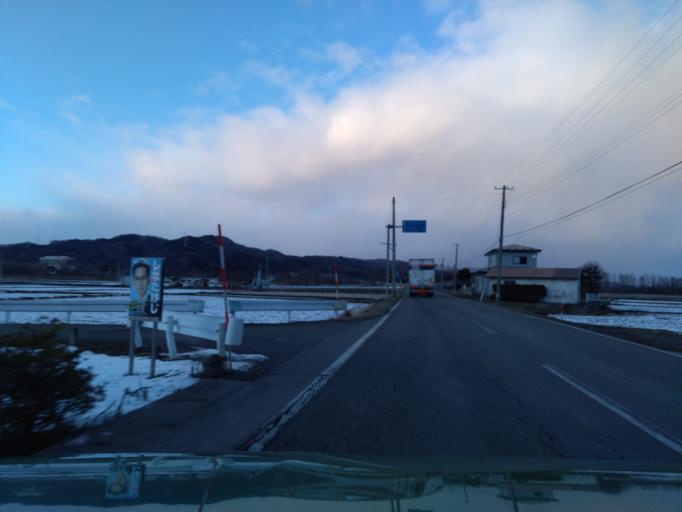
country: JP
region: Iwate
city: Shizukuishi
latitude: 39.6916
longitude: 141.0653
